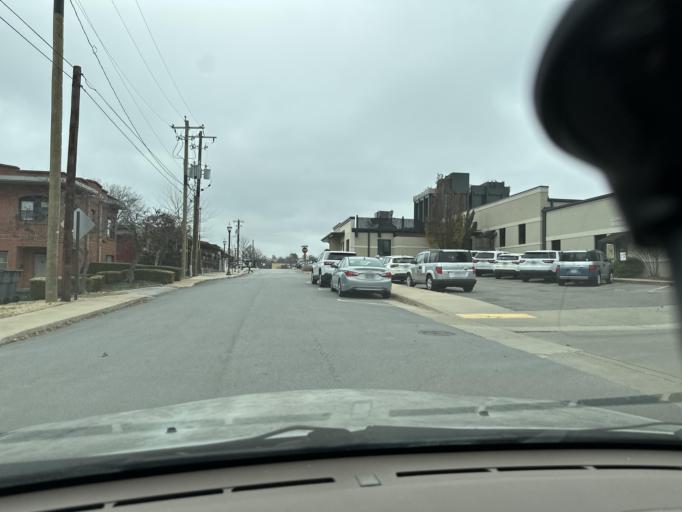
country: US
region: Arkansas
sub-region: Washington County
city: Fayetteville
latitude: 36.0613
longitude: -94.1619
